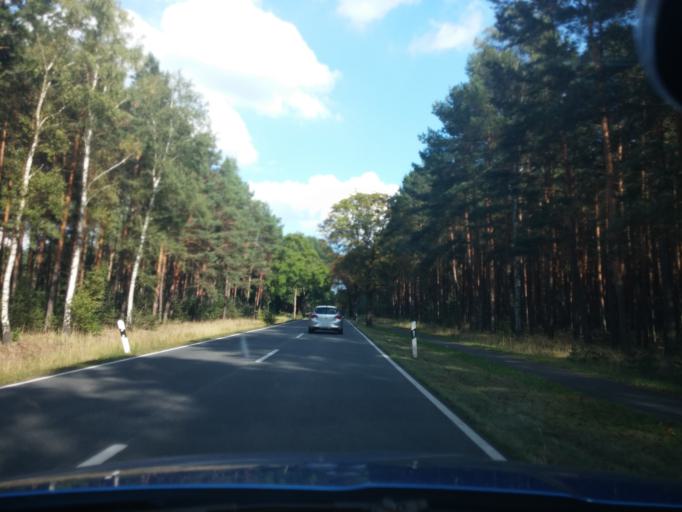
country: DE
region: Brandenburg
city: Halbe
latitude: 52.1068
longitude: 13.7185
